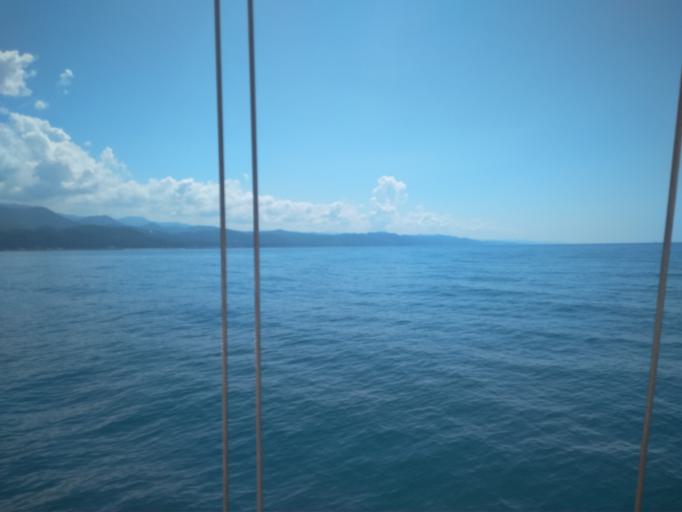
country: RU
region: Krasnodarskiy
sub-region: Sochi City
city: Lazarevskoye
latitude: 43.8736
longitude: 39.3165
